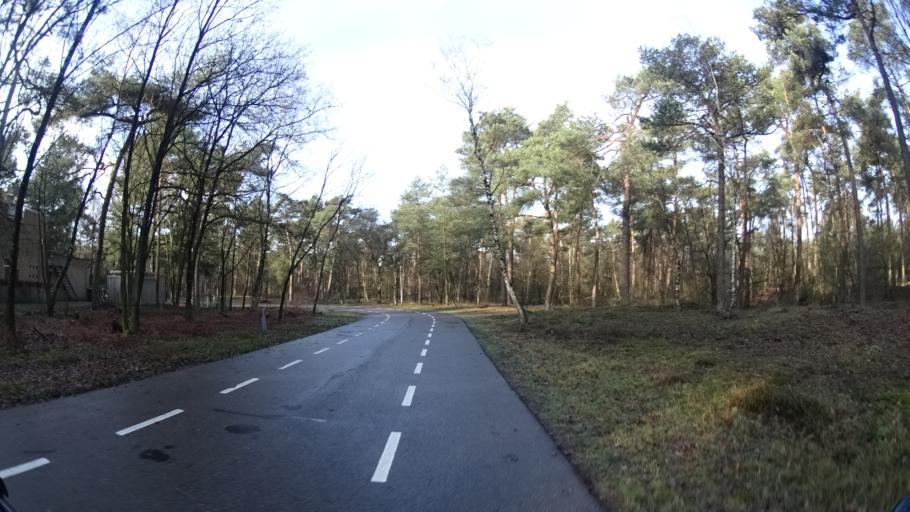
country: NL
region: Gelderland
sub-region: Gemeente Ede
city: Wekerom
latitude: 52.0919
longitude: 5.7356
